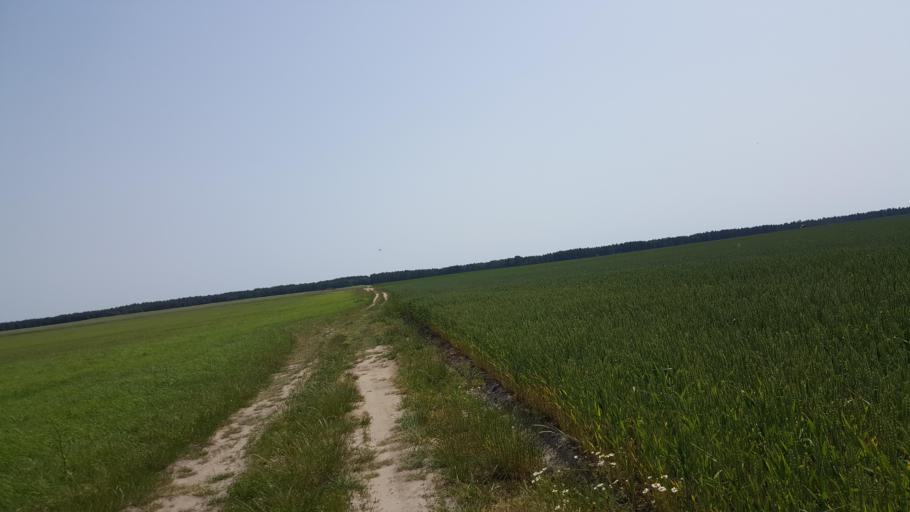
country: BY
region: Brest
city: Kamyanyuki
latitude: 52.4930
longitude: 23.8491
